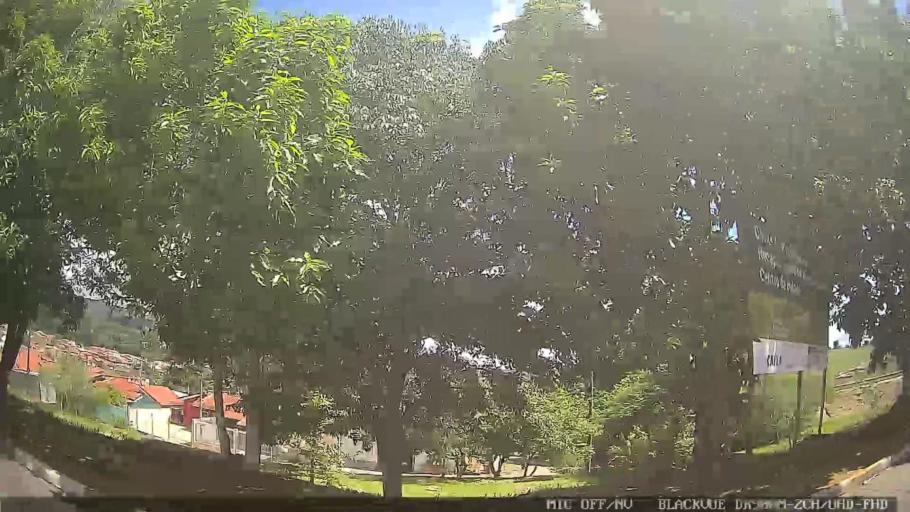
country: BR
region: Sao Paulo
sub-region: Amparo
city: Amparo
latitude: -22.8152
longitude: -46.6914
